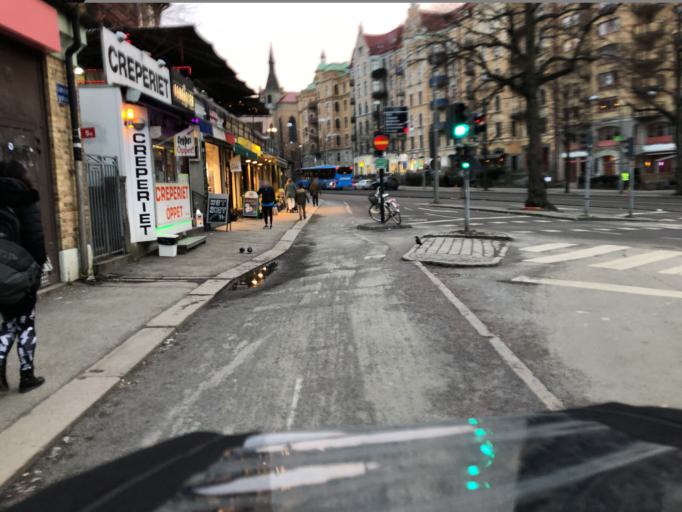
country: SE
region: Vaestra Goetaland
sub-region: Goteborg
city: Goeteborg
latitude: 57.6963
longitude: 11.9519
